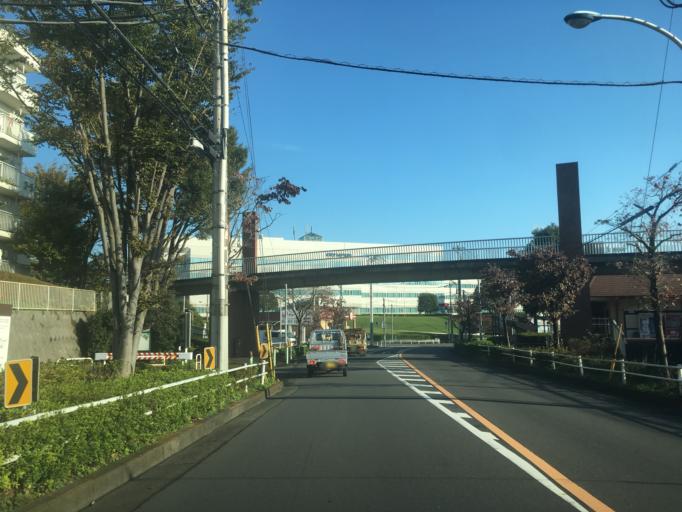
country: JP
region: Tokyo
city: Hino
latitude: 35.6874
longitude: 139.3590
